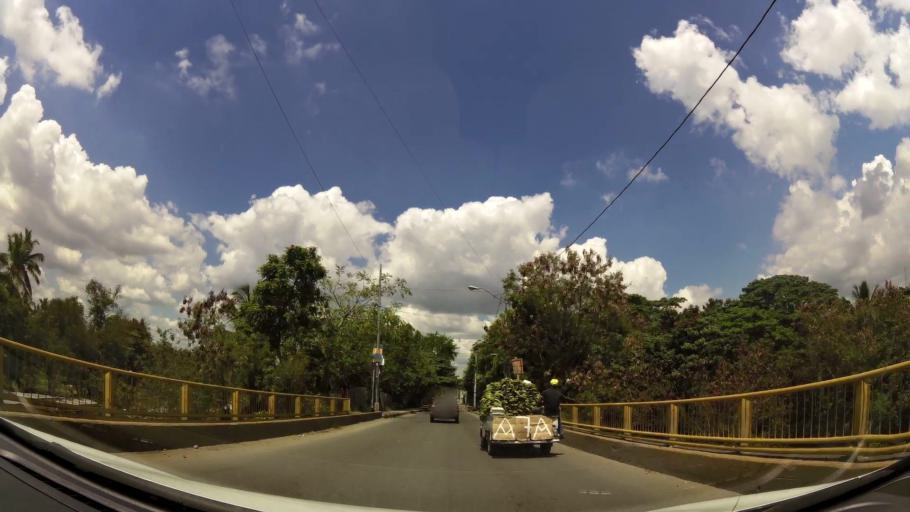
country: DO
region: Santo Domingo
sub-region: Santo Domingo
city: Santo Domingo Este
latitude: 18.5198
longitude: -69.8688
